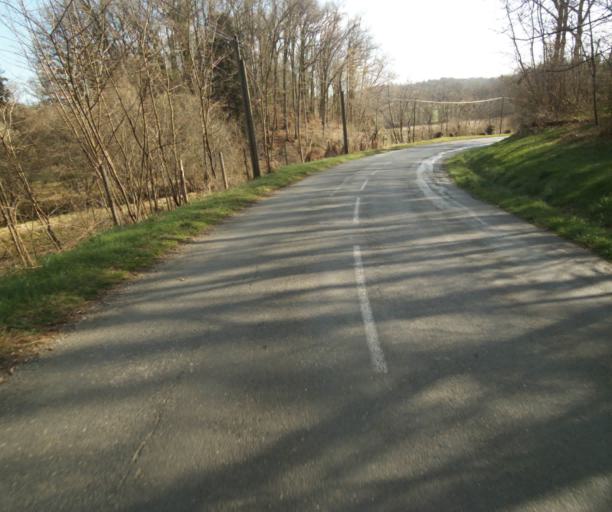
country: FR
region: Limousin
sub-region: Departement de la Correze
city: Saint-Clement
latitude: 45.3460
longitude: 1.6250
